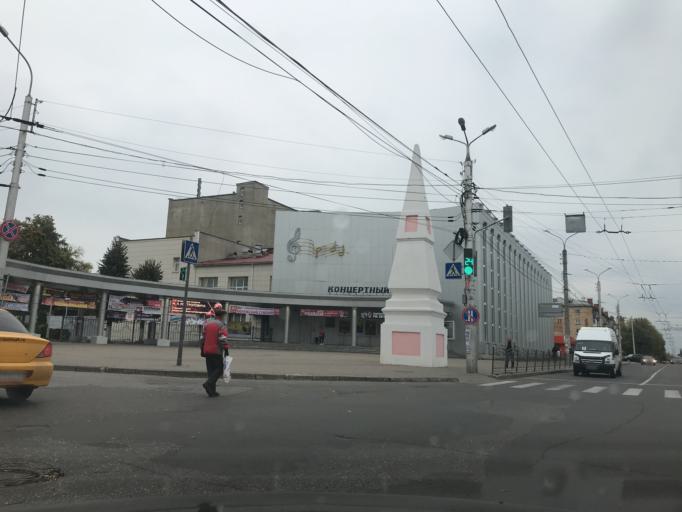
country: RU
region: Kaluga
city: Kaluga
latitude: 54.5194
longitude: 36.2677
